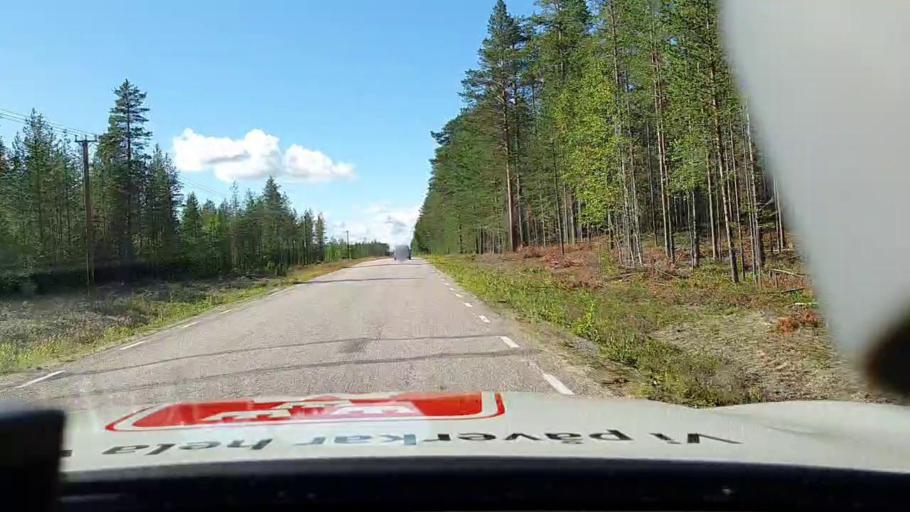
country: SE
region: Norrbotten
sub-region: Overkalix Kommun
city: OEverkalix
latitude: 66.2515
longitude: 22.8765
